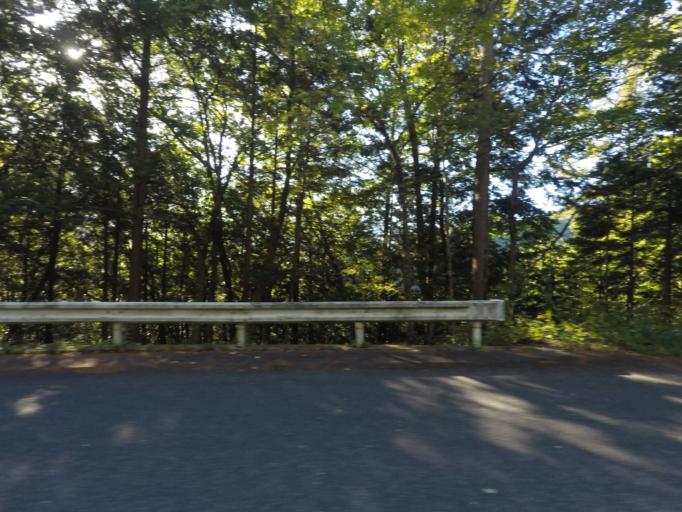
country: JP
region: Nagano
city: Tatsuno
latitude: 35.9703
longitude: 137.7738
